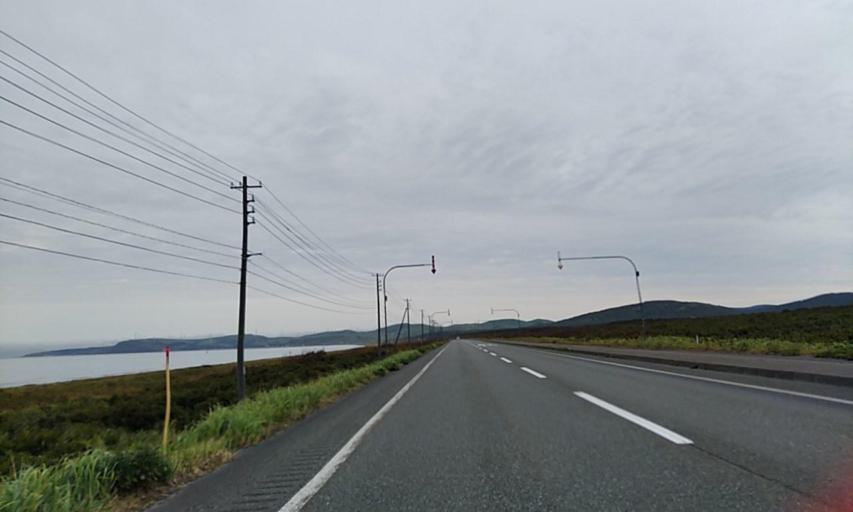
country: JP
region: Hokkaido
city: Makubetsu
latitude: 45.4158
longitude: 141.8281
